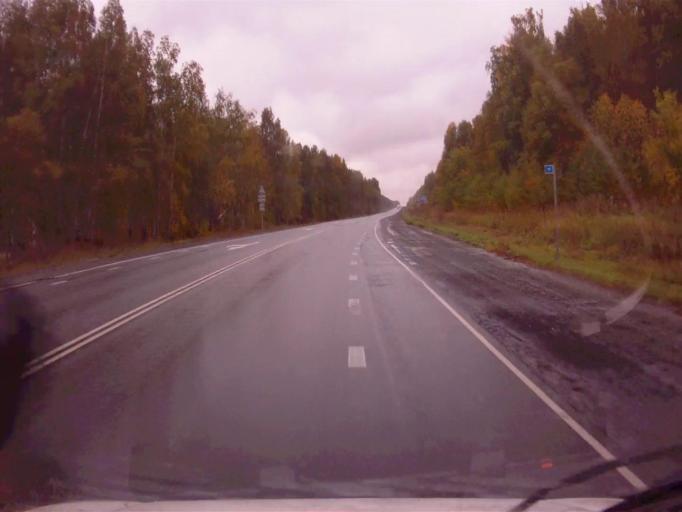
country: RU
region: Chelyabinsk
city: Roshchino
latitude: 55.3719
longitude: 61.1576
